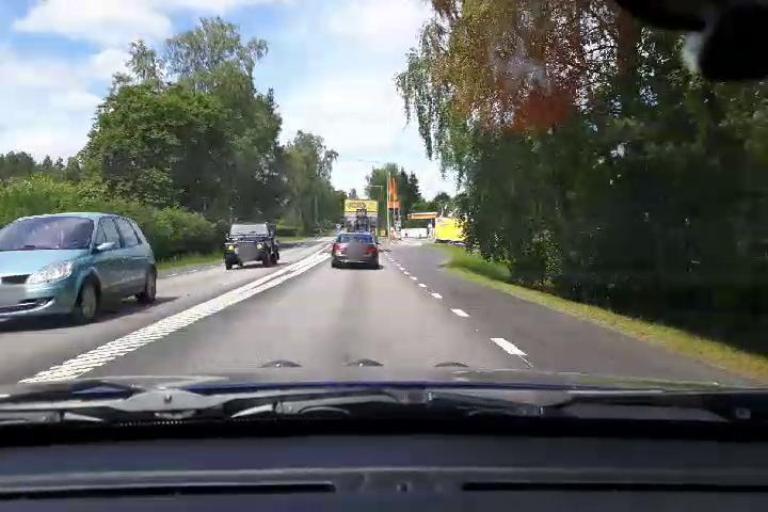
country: SE
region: Uppsala
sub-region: Osthammars Kommun
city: Bjorklinge
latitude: 60.0357
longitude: 17.5515
